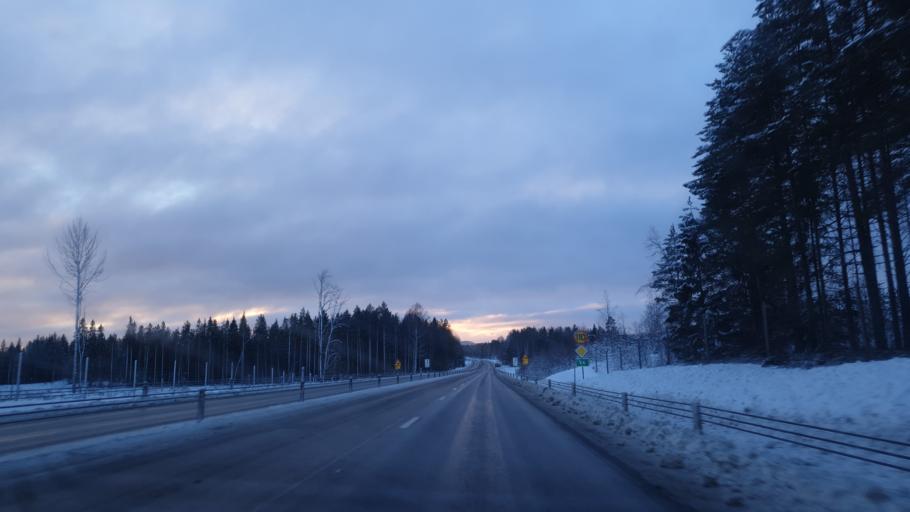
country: SE
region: Vaesternorrland
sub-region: OErnskoeldsviks Kommun
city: Husum
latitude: 63.4862
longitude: 19.3065
